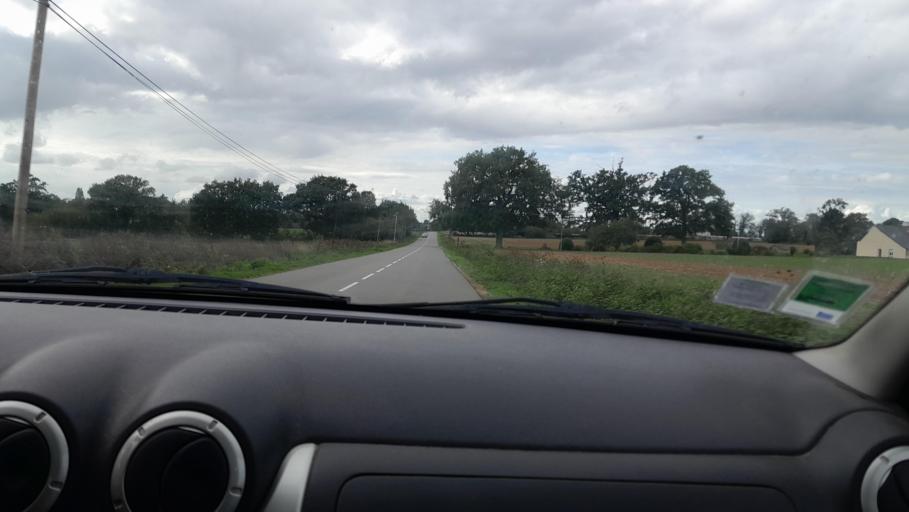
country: FR
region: Brittany
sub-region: Departement d'Ille-et-Vilaine
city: Argentre-du-Plessis
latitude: 48.0541
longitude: -1.1221
